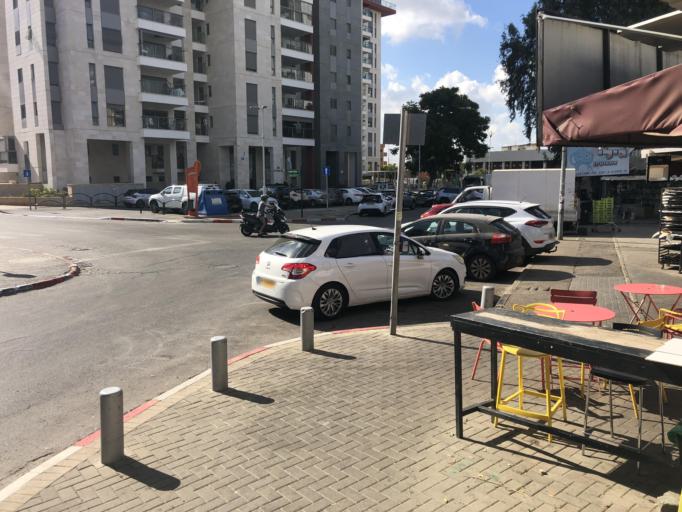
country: IL
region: Central District
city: Yehud
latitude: 32.0293
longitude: 34.8889
